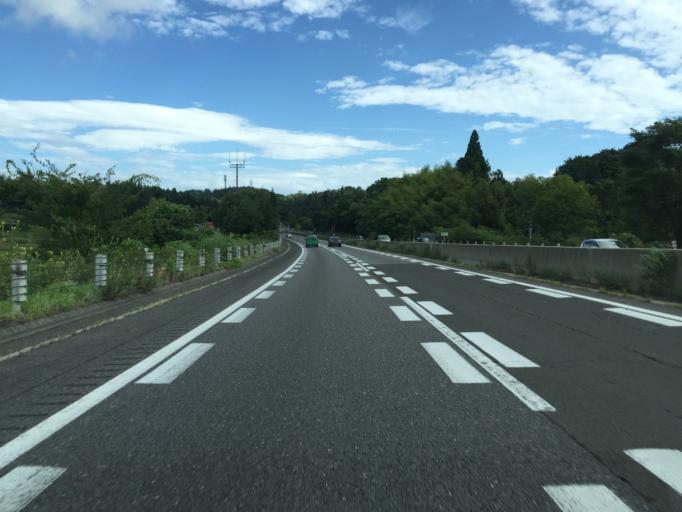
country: JP
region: Fukushima
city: Nihommatsu
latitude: 37.6431
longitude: 140.4343
